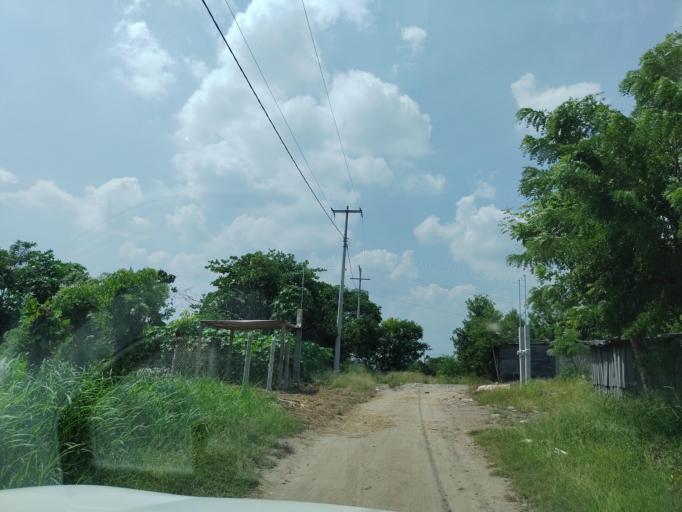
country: MX
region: Veracruz
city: Martinez de la Torre
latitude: 20.0772
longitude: -97.0450
